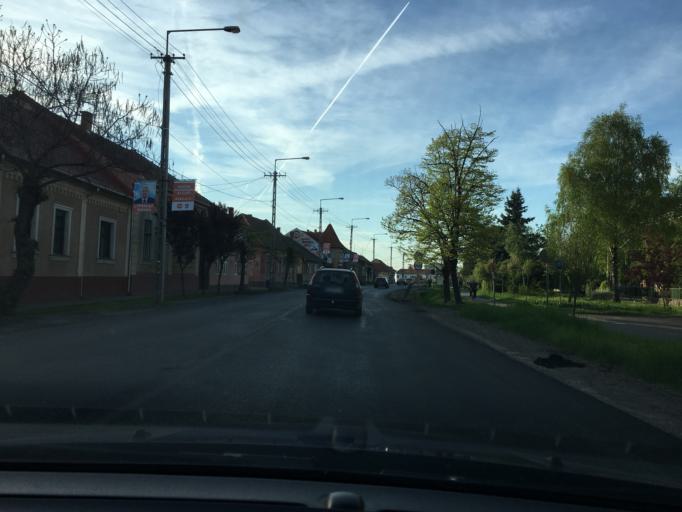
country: HU
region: Hajdu-Bihar
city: Berettyoujfalu
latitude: 47.2266
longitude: 21.5344
